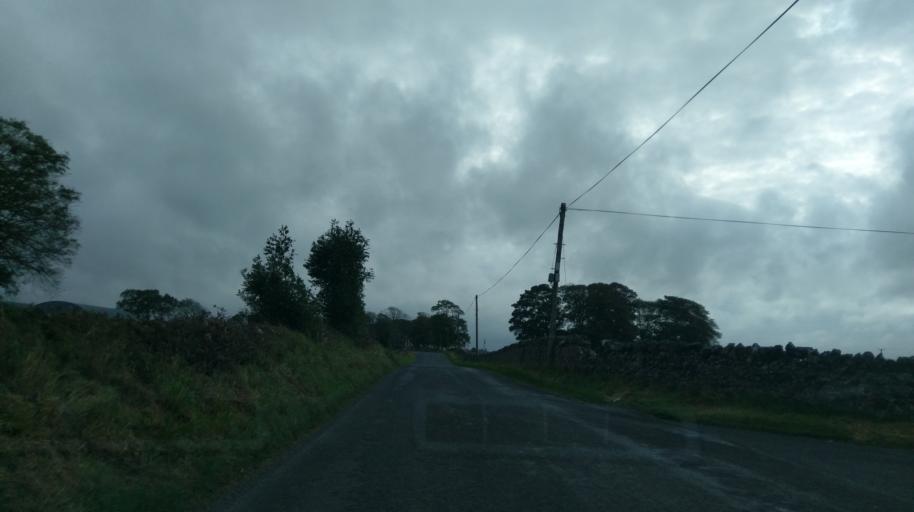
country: IE
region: Connaught
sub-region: County Galway
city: Athenry
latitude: 53.4545
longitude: -8.5881
